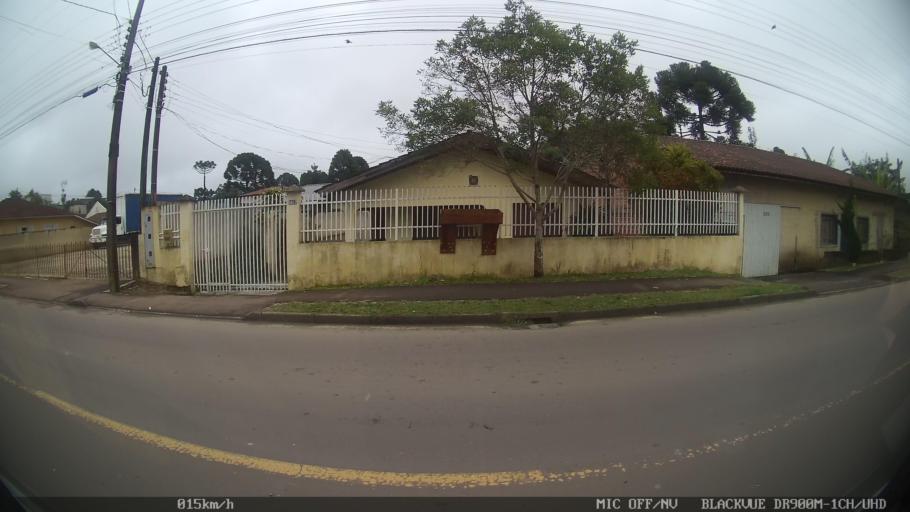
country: BR
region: Parana
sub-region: Sao Jose Dos Pinhais
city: Sao Jose dos Pinhais
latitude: -25.5840
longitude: -49.1712
